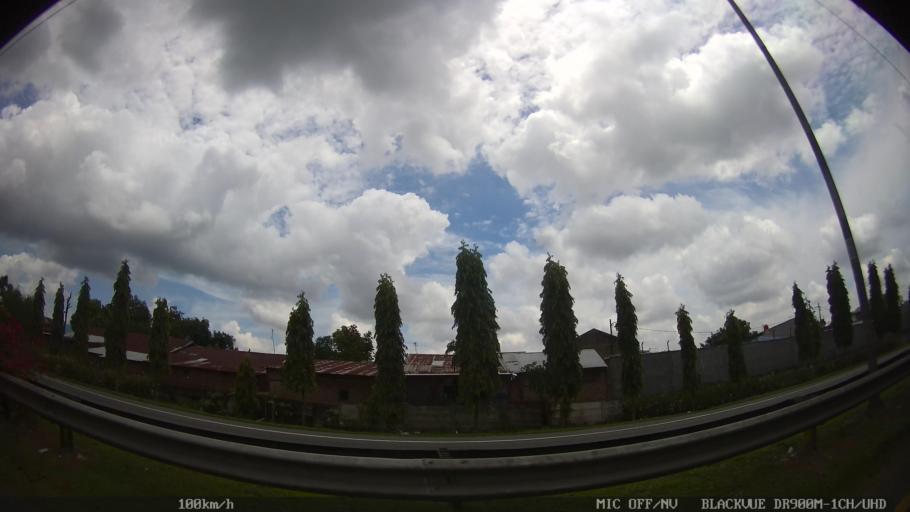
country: ID
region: North Sumatra
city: Medan
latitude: 3.6171
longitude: 98.7208
